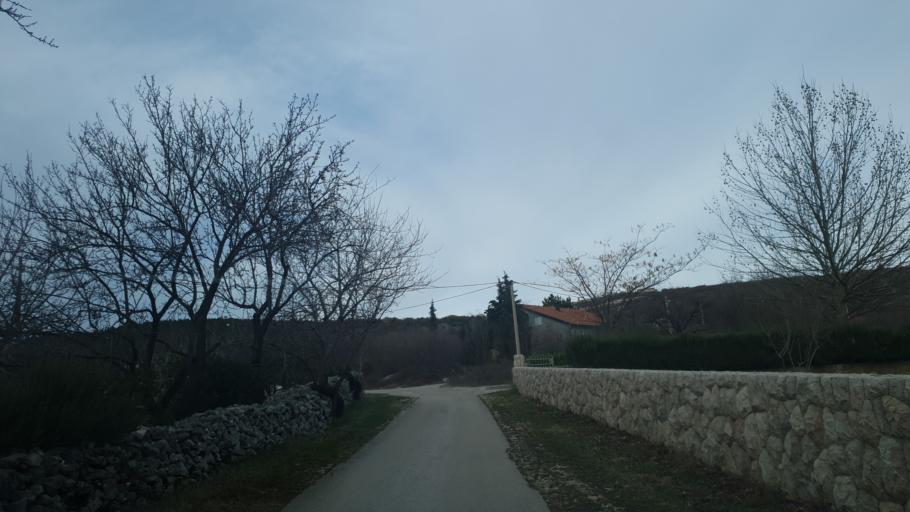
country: HR
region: Splitsko-Dalmatinska
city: Imotski
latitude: 43.4446
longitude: 17.2345
